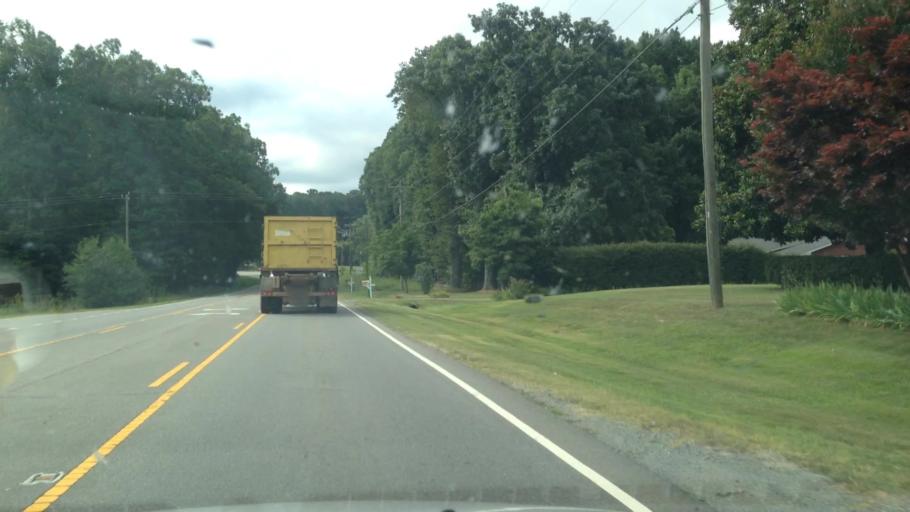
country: US
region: North Carolina
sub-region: Rockingham County
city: Wentworth
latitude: 36.3937
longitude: -79.7558
